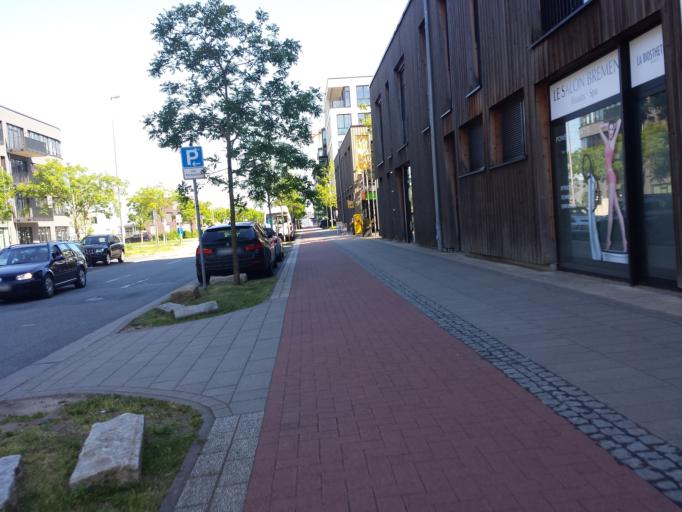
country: DE
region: Bremen
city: Bremen
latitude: 53.0977
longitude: 8.7606
